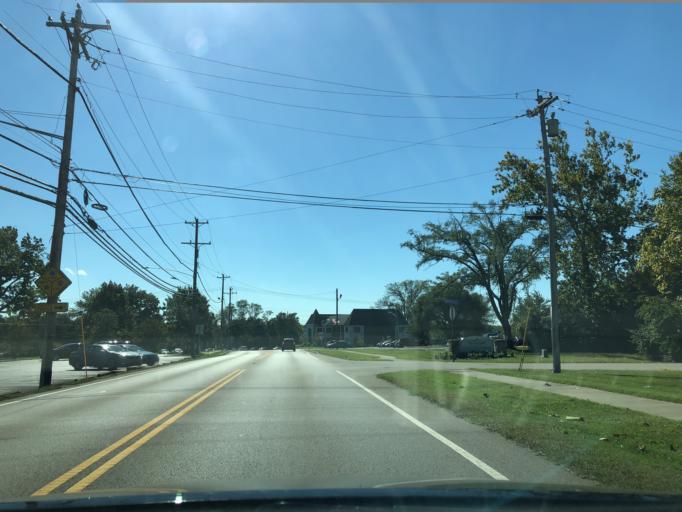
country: US
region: Ohio
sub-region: Hamilton County
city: Sixteen Mile Stand
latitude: 39.2851
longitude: -84.3164
